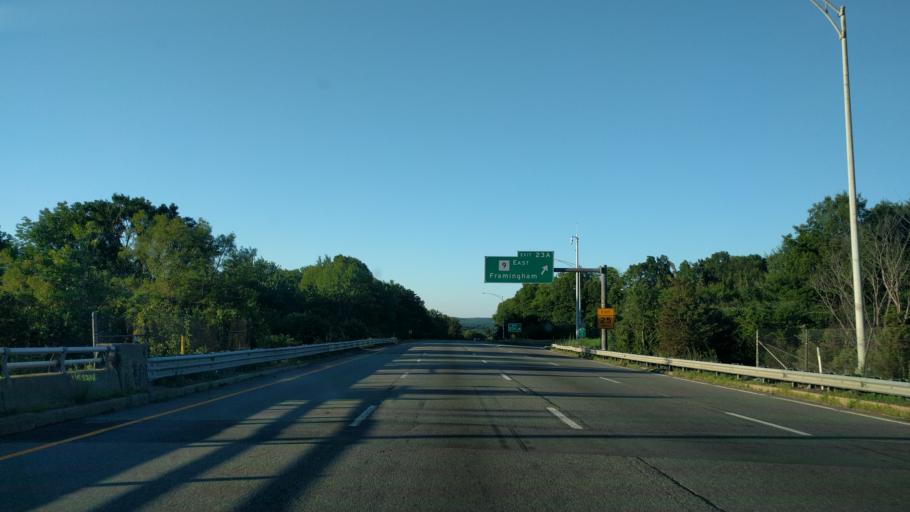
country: US
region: Massachusetts
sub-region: Worcester County
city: Southborough
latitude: 42.2886
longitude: -71.5675
